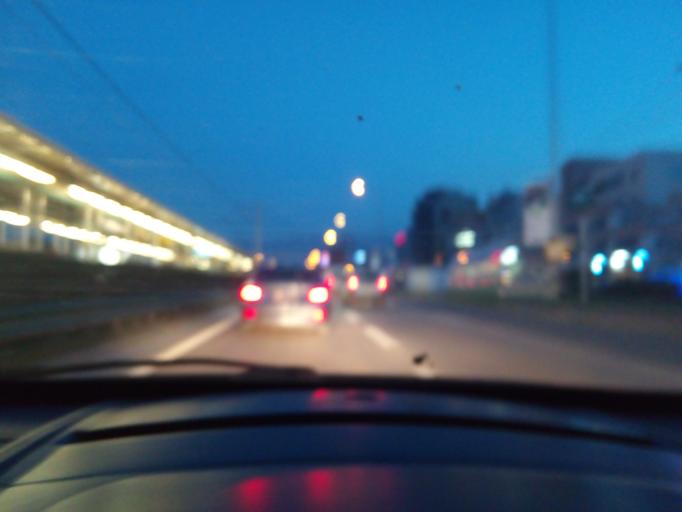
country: TR
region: Bursa
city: Niluefer
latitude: 40.2372
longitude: 28.9751
